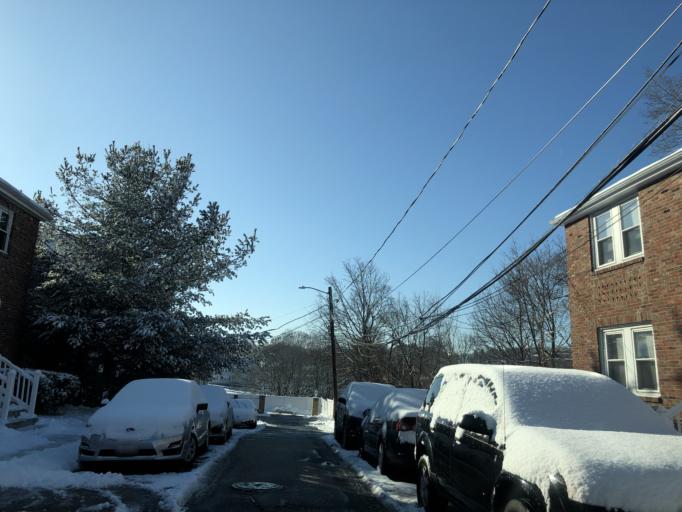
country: US
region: Massachusetts
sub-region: Middlesex County
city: Watertown
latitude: 42.3484
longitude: -71.1582
